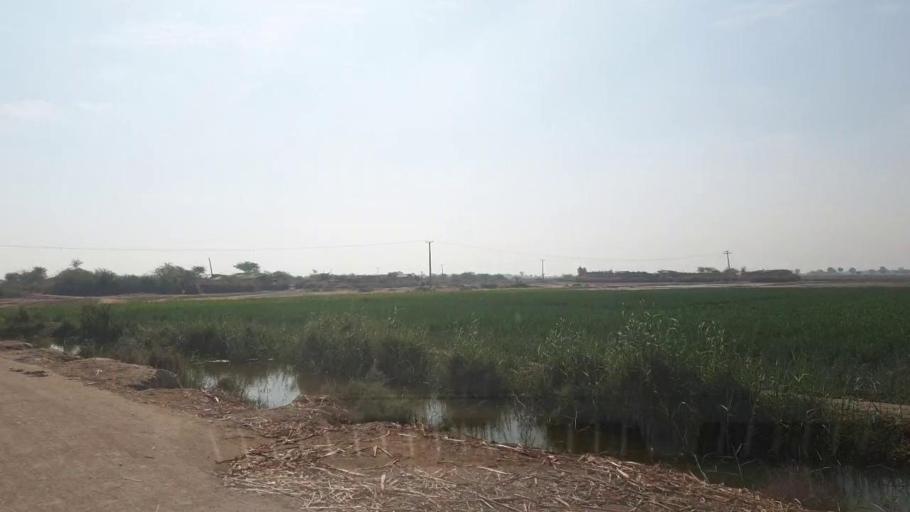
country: PK
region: Sindh
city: Mirwah Gorchani
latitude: 25.3678
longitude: 69.1862
